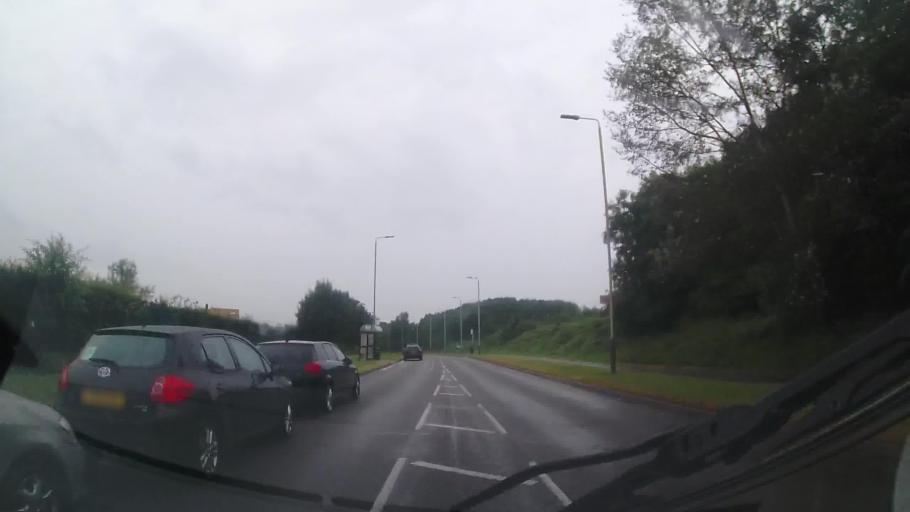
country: GB
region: England
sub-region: Leicestershire
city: Anstey
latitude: 52.6752
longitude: -1.1553
